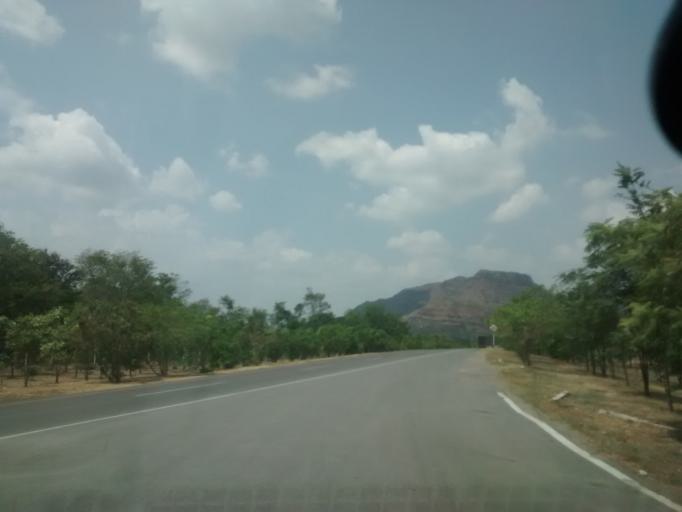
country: CO
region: Tolima
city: Valle de San Juan
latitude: 4.2724
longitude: -75.0004
